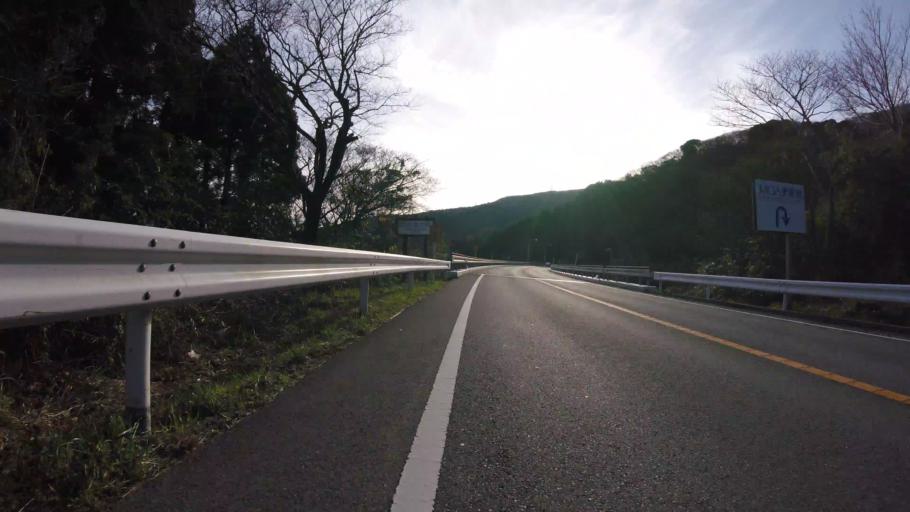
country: JP
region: Shizuoka
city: Atami
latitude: 35.1128
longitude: 139.0471
